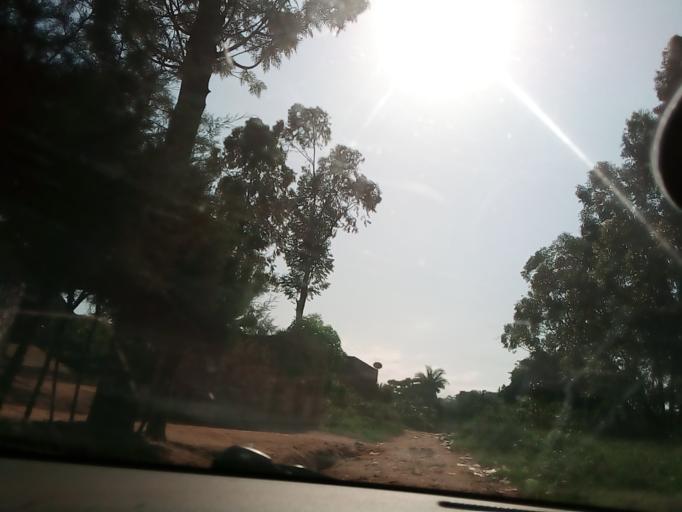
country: UG
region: Central Region
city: Masaka
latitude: -0.3390
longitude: 31.7265
